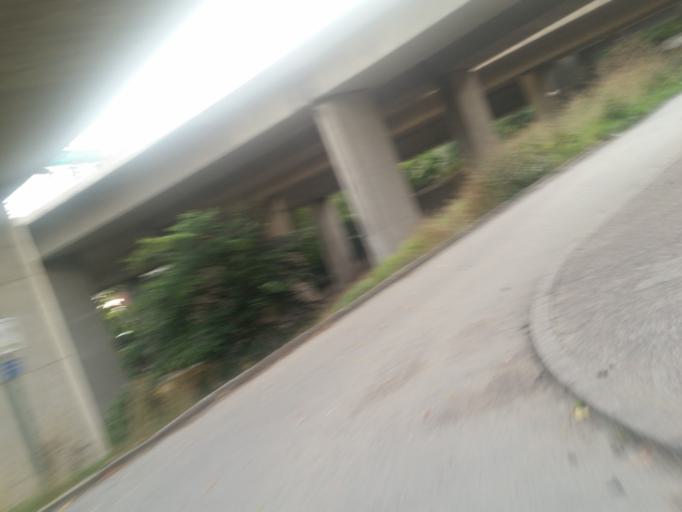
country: SE
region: Stockholm
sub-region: Solna Kommun
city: Solna
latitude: 59.3208
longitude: 17.9974
